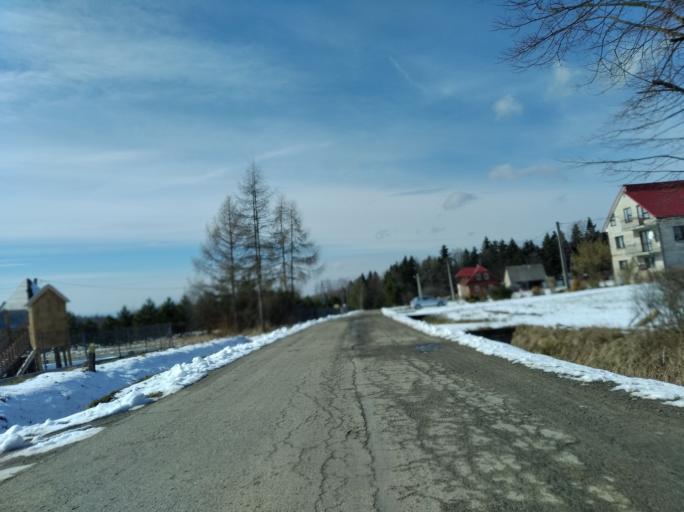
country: PL
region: Subcarpathian Voivodeship
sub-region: Powiat krosnienski
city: Korczyna
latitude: 49.7473
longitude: 21.8181
